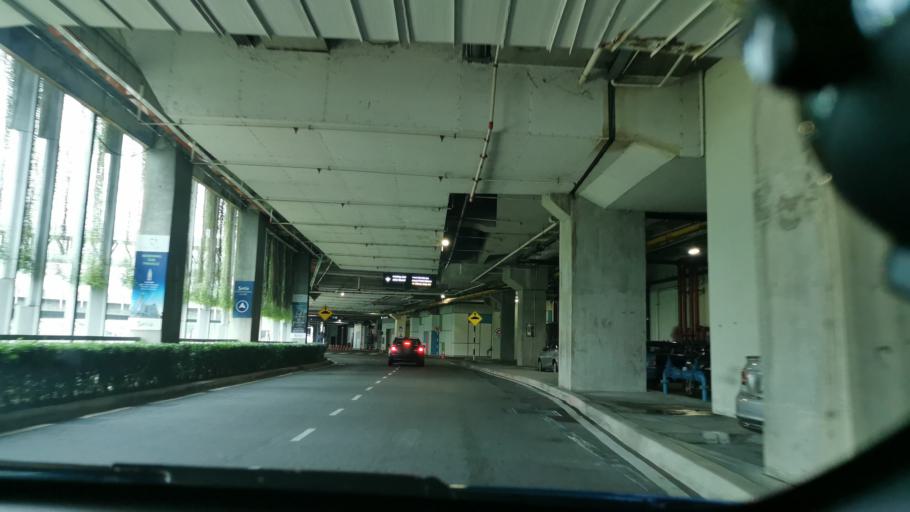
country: MY
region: Kuala Lumpur
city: Kuala Lumpur
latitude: 3.1197
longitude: 101.6746
